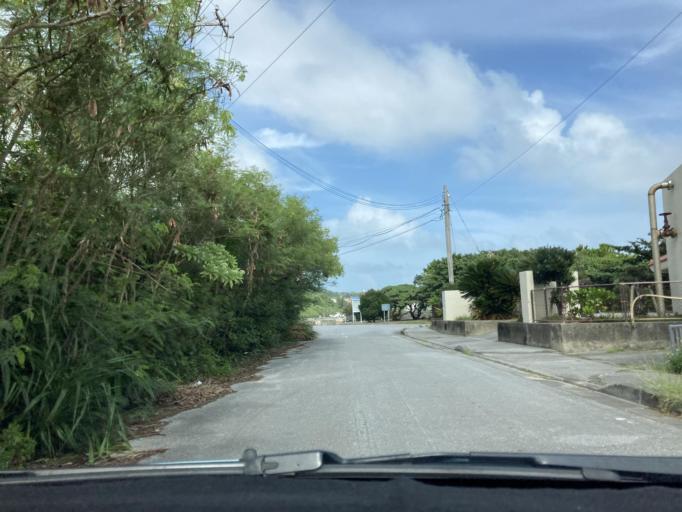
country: JP
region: Okinawa
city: Ginowan
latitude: 26.1510
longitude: 127.8076
